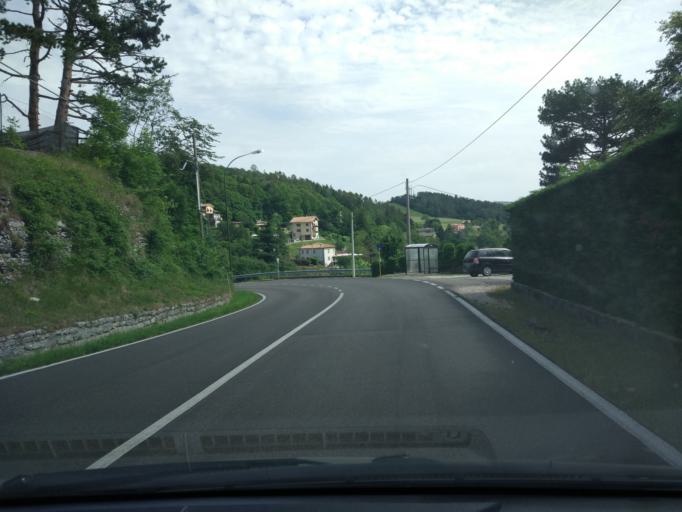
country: IT
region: Veneto
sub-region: Provincia di Verona
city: Ferrara di Monte Baldo
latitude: 45.6443
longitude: 10.8531
